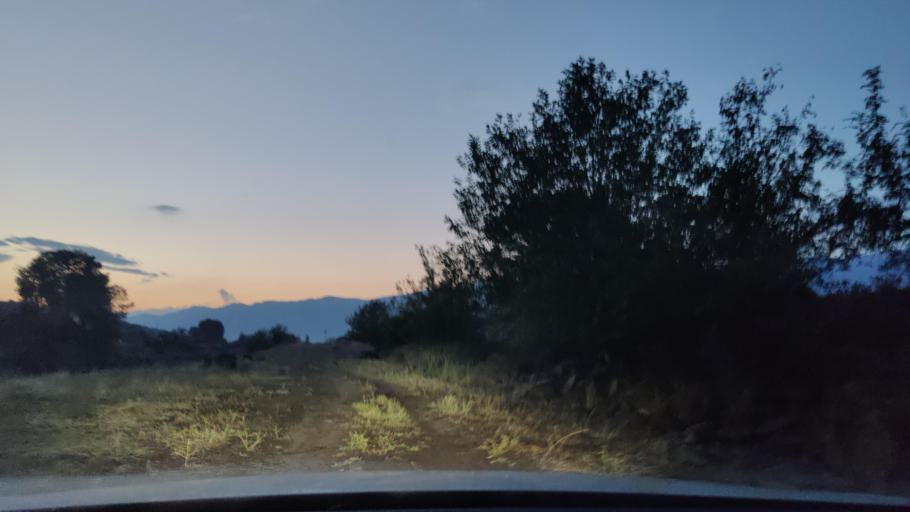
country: GR
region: Central Macedonia
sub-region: Nomos Serron
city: Chrysochorafa
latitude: 41.2036
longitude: 23.0788
